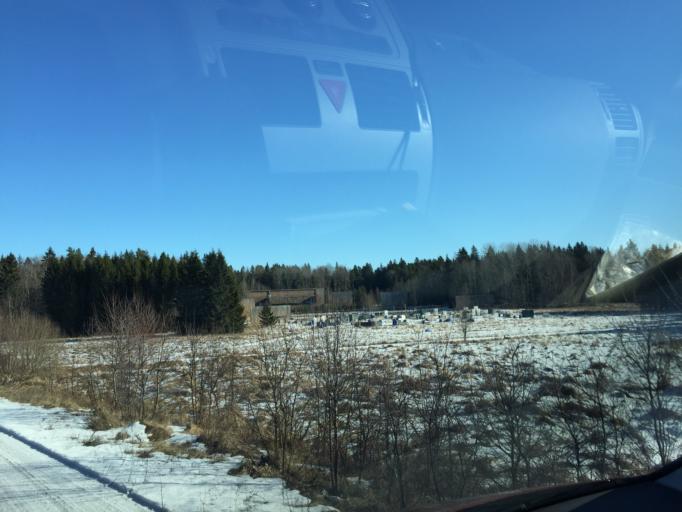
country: SE
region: Stockholm
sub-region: Sodertalje Kommun
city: Soedertaelje
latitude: 59.1670
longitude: 17.5339
